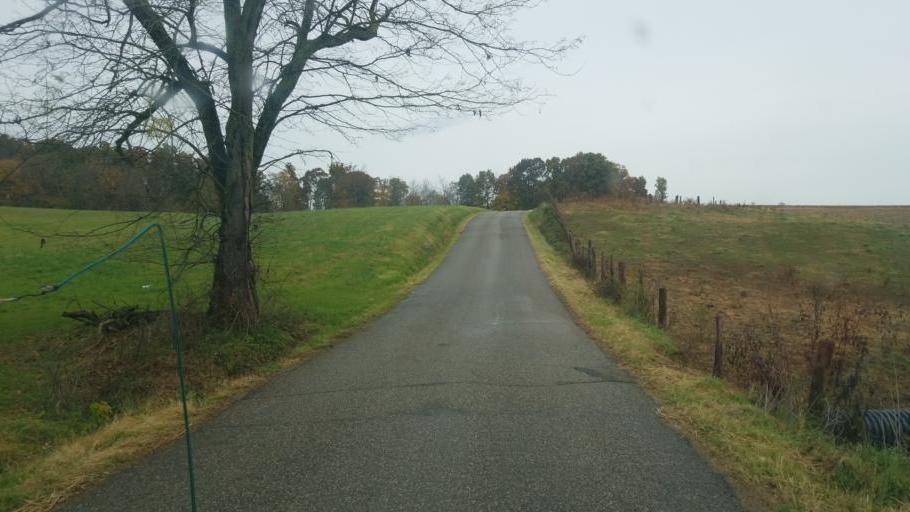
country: US
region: Ohio
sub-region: Washington County
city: Beverly
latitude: 39.5390
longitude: -81.7083
